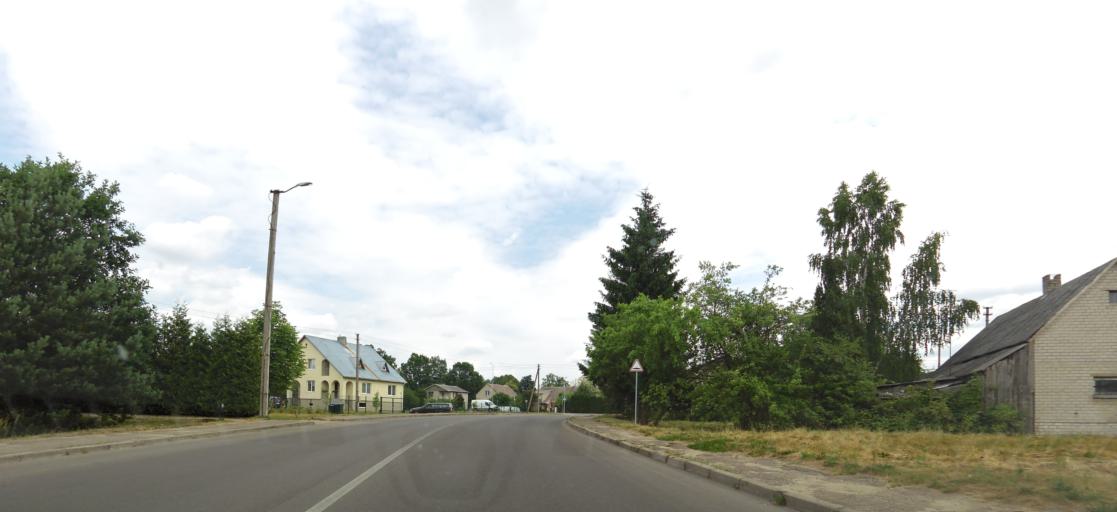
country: LT
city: Sirvintos
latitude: 55.0406
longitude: 24.9685
